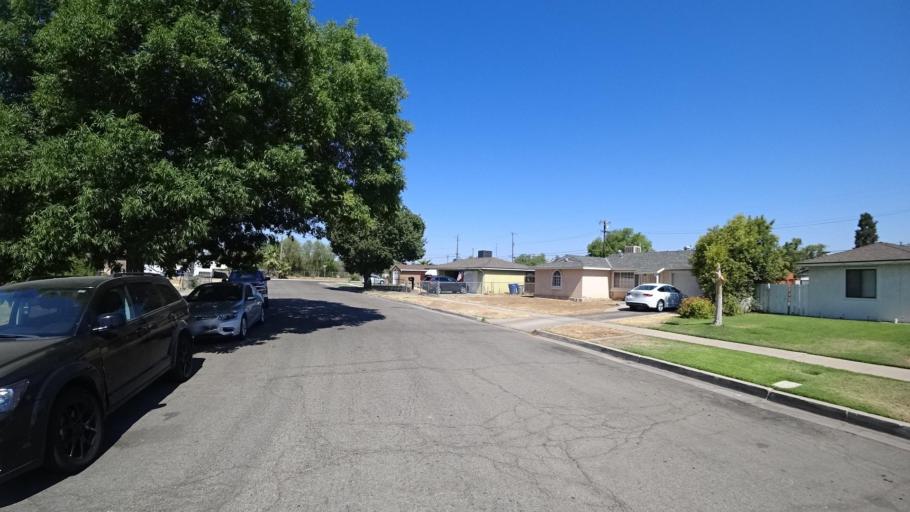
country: US
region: California
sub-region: Fresno County
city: Fresno
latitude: 36.7998
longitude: -119.7839
